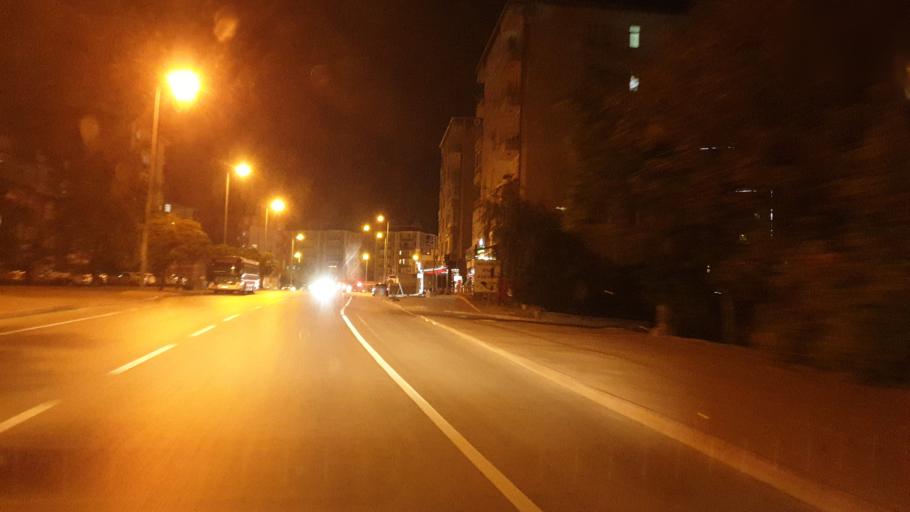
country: TR
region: Kayseri
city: Talas
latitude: 38.6957
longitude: 35.5456
